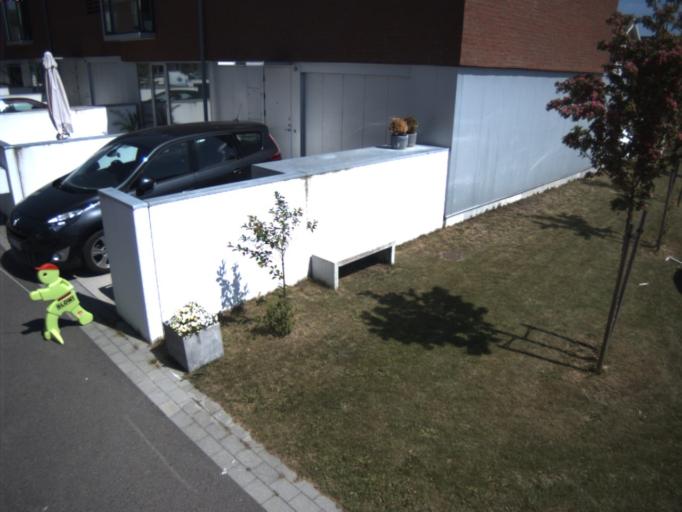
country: SE
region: Skane
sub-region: Helsingborg
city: Rydeback
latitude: 56.0070
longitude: 12.7543
